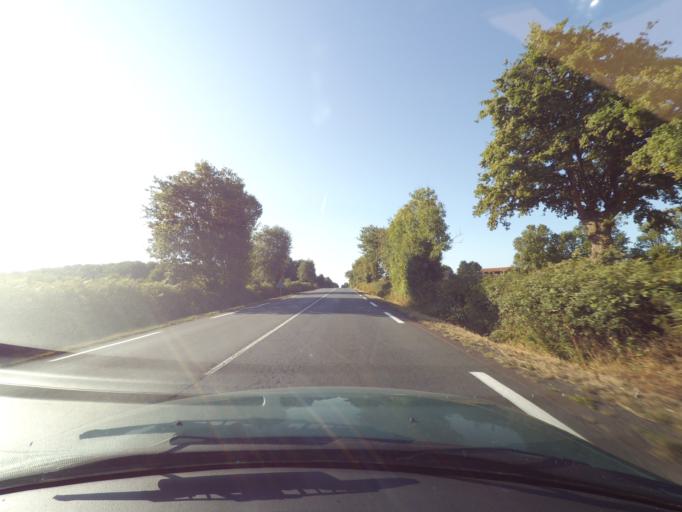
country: FR
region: Poitou-Charentes
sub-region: Departement des Deux-Sevres
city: Viennay
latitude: 46.7214
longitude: -0.2975
